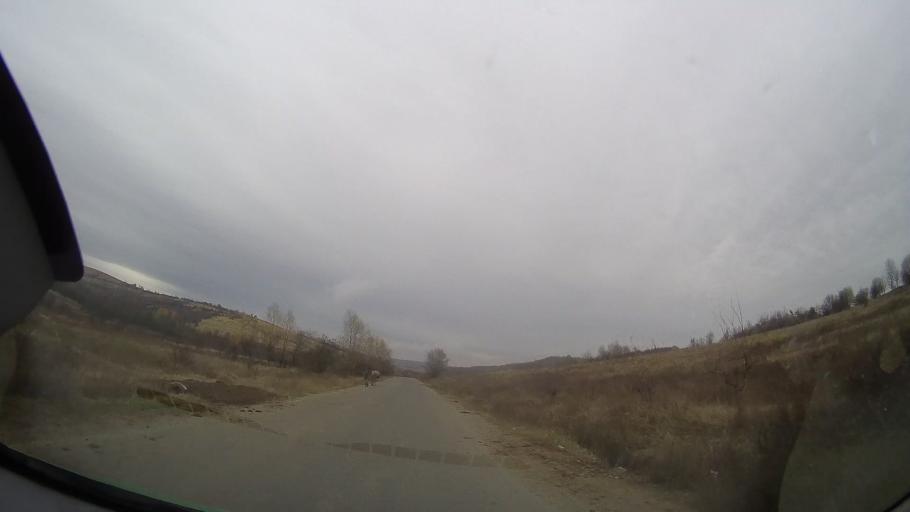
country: RO
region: Prahova
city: Mocesti
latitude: 45.0612
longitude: 26.2678
